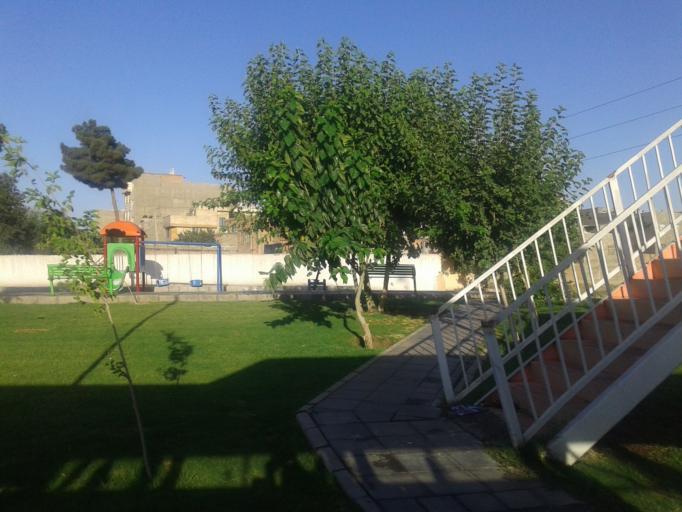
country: IR
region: Tehran
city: Rey
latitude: 35.6245
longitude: 51.3614
